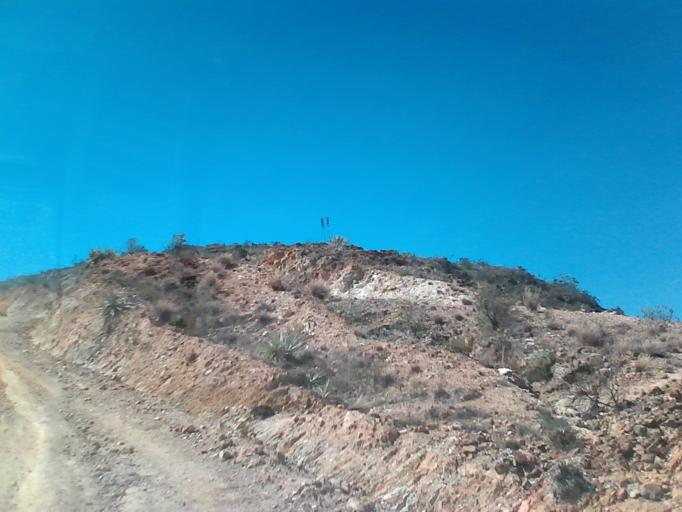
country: CO
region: Boyaca
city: Sachica
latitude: 5.5433
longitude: -73.5561
